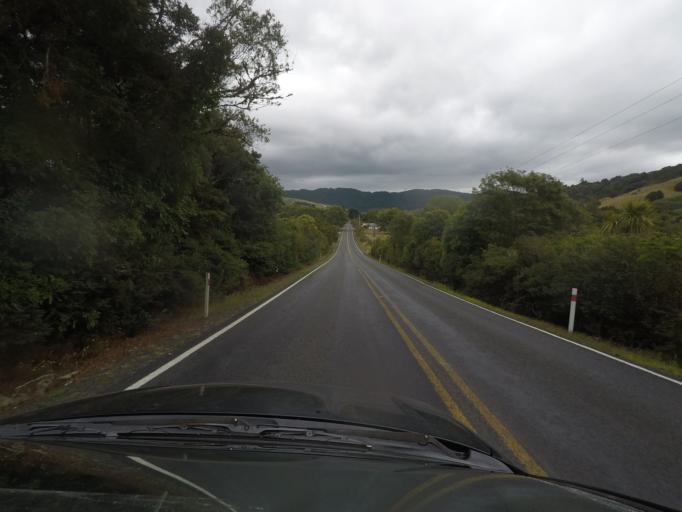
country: NZ
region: Auckland
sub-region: Auckland
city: Wellsford
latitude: -36.2829
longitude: 174.6359
